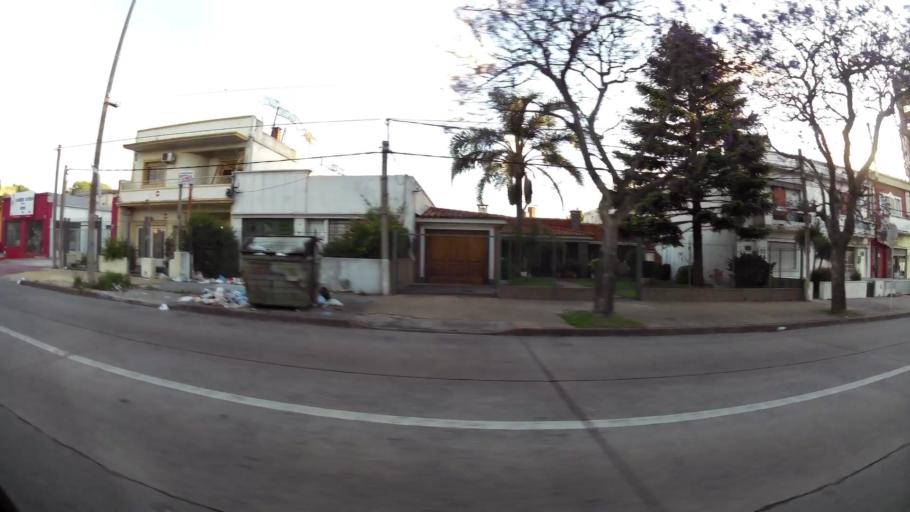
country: UY
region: Montevideo
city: Montevideo
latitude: -34.8868
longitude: -56.1322
